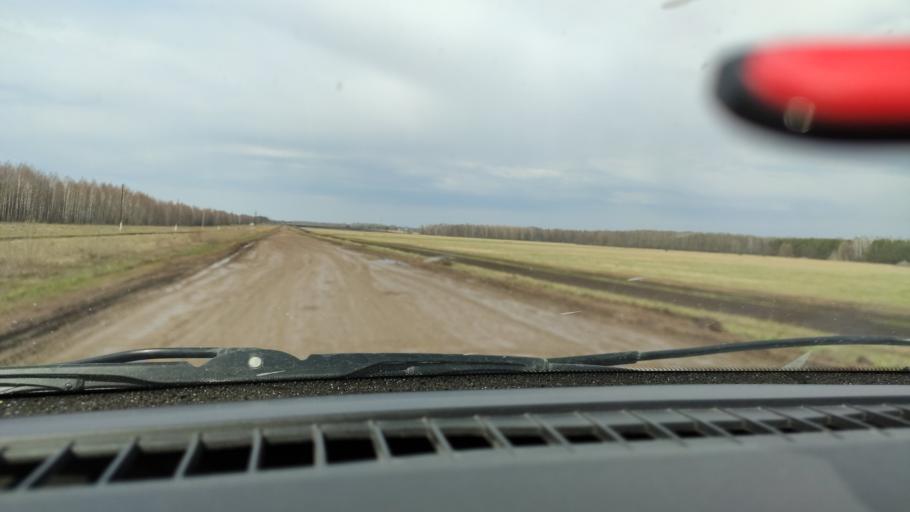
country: RU
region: Bashkortostan
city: Burayevo
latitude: 55.6537
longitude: 55.1829
